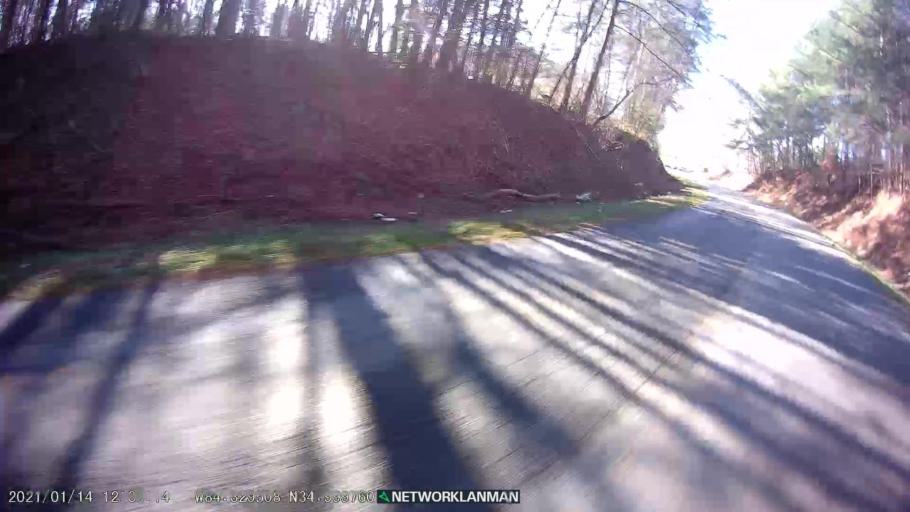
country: US
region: Georgia
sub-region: Fannin County
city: McCaysville
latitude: 34.9998
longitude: -84.3297
